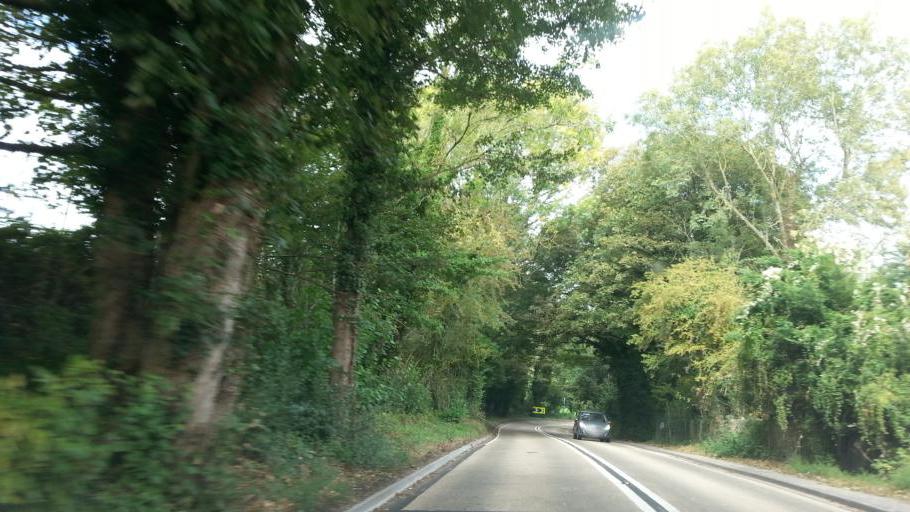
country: GB
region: England
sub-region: Gloucestershire
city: Stroud
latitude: 51.7618
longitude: -2.2221
